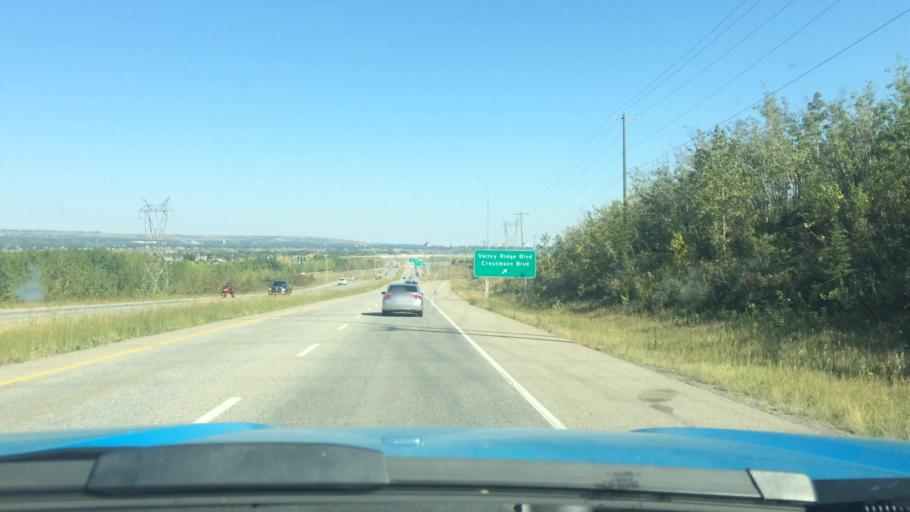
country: CA
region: Alberta
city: Calgary
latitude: 51.0885
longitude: -114.2576
